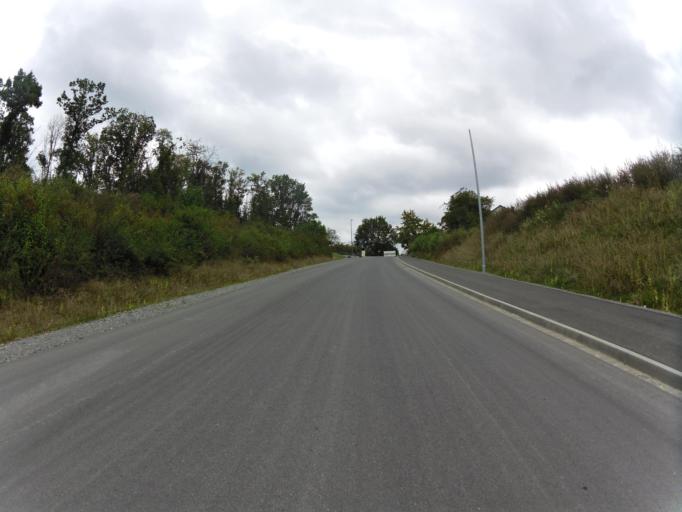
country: DE
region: Bavaria
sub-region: Regierungsbezirk Unterfranken
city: Randersacker
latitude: 49.7534
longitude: 9.9542
